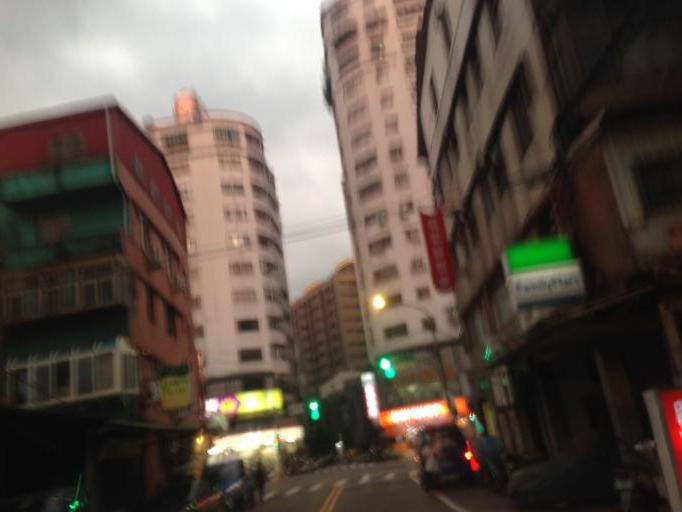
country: TW
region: Taiwan
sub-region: Taoyuan
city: Taoyuan
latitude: 24.9369
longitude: 121.3755
